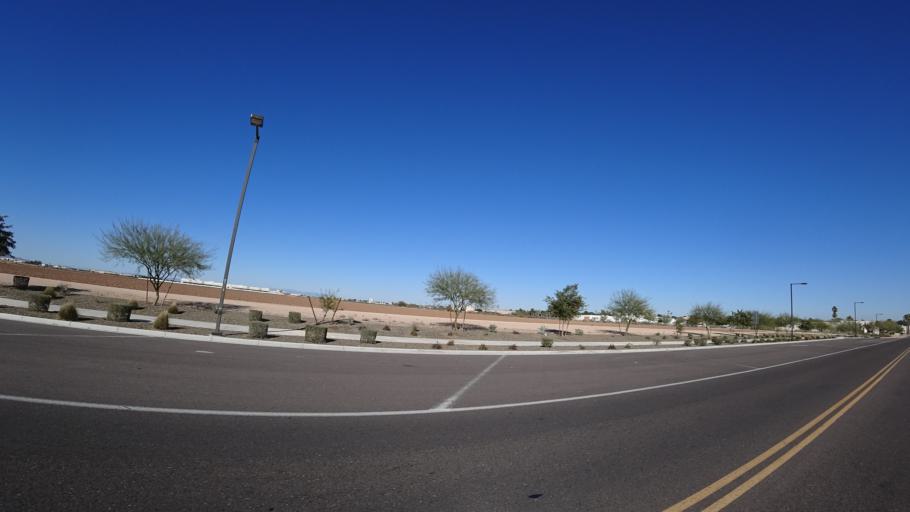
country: US
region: Arizona
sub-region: Maricopa County
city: Goodyear
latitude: 33.4354
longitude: -112.3646
